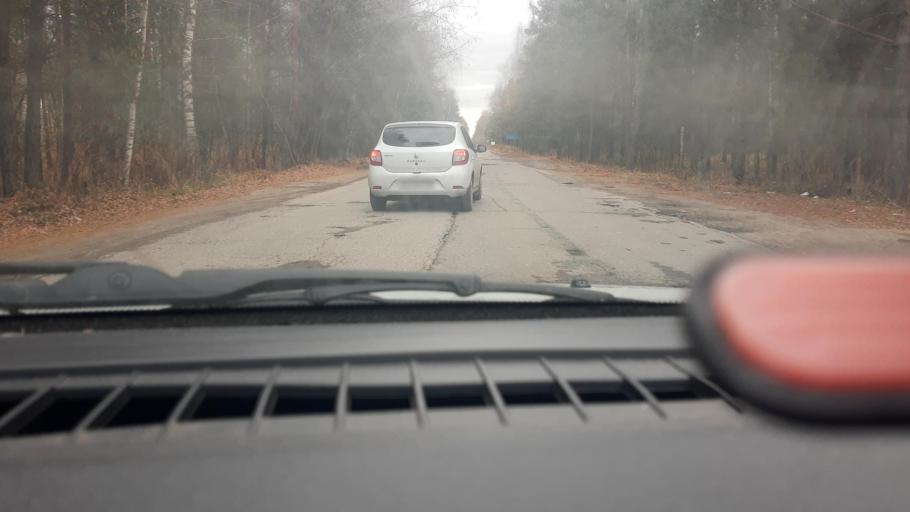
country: RU
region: Nizjnij Novgorod
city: Babino
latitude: 56.3039
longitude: 43.6623
